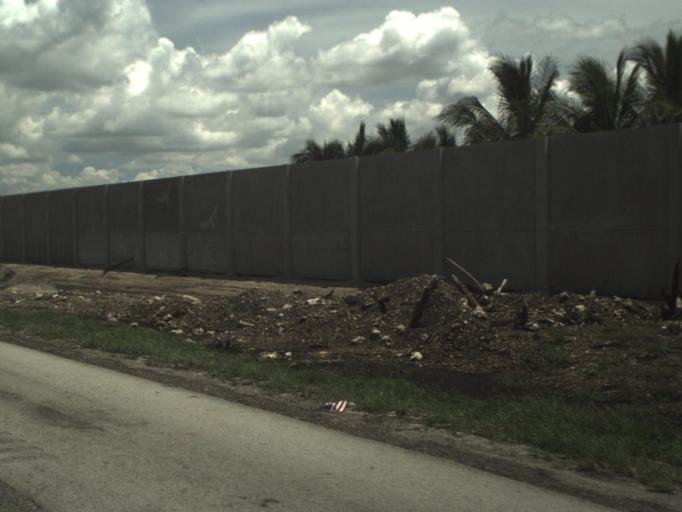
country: US
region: Florida
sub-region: Broward County
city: Southwest Ranches
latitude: 26.0499
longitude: -80.3526
